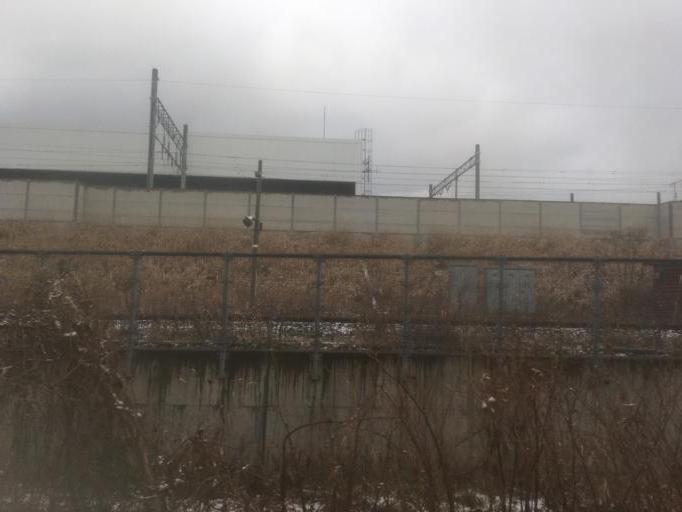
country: JP
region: Aomori
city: Goshogawara
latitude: 41.1437
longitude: 140.5161
